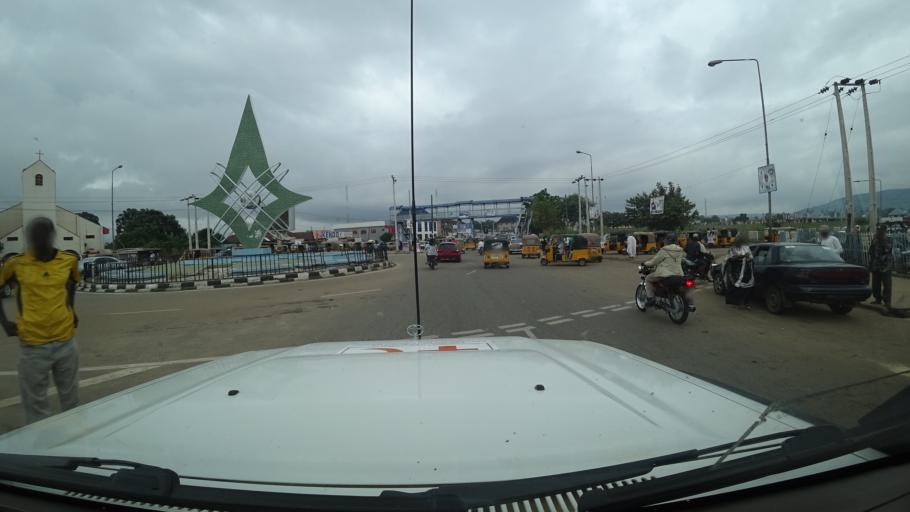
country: NG
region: Niger
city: Minna
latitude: 9.6142
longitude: 6.5476
